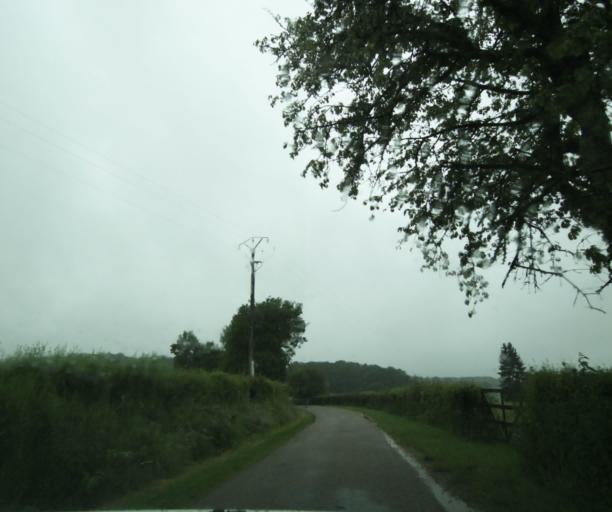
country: FR
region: Bourgogne
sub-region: Departement de Saone-et-Loire
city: Charolles
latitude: 46.4074
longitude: 4.2567
